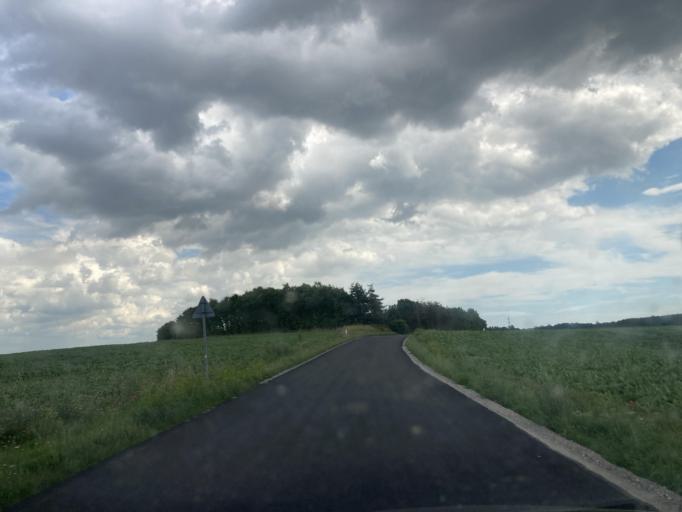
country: DK
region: Zealand
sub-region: Faxe Kommune
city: Haslev
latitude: 55.3350
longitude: 11.9954
